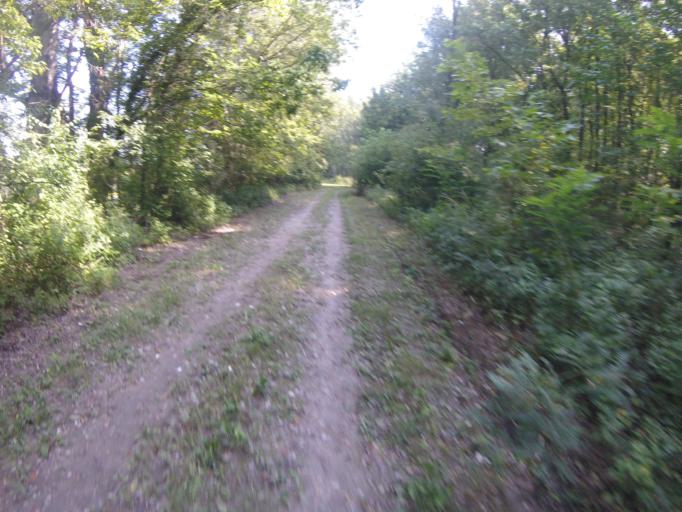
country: HU
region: Bacs-Kiskun
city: Baja
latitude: 46.2240
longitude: 18.8800
